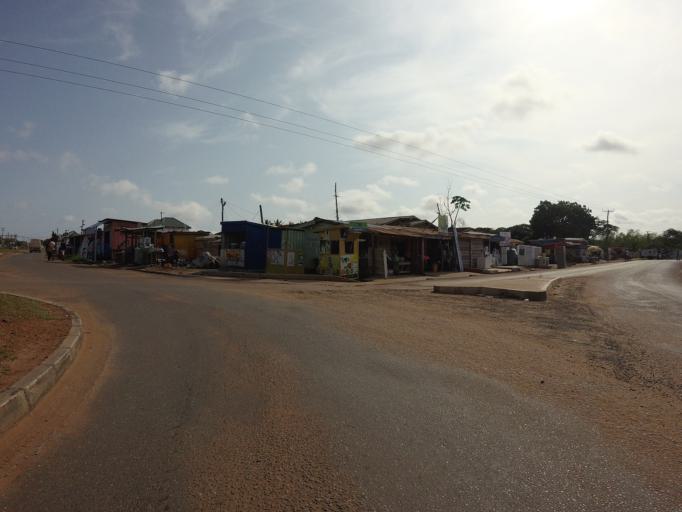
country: GH
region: Greater Accra
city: Nungua
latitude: 5.6430
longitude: -0.1007
